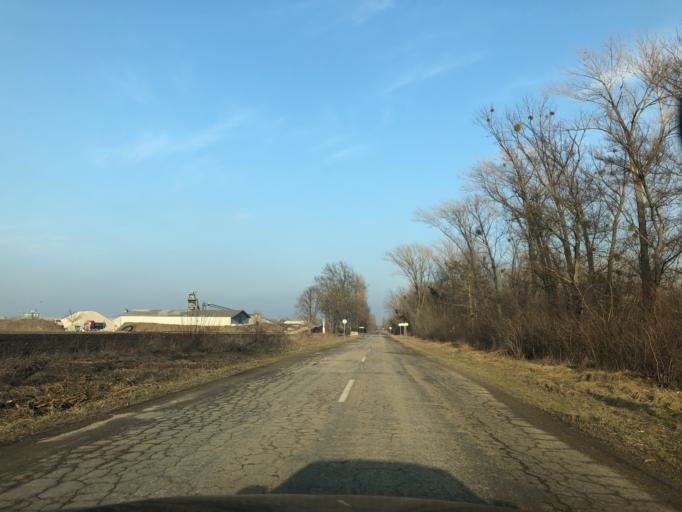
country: HU
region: Gyor-Moson-Sopron
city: Kapuvar
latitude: 47.5797
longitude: 17.0821
